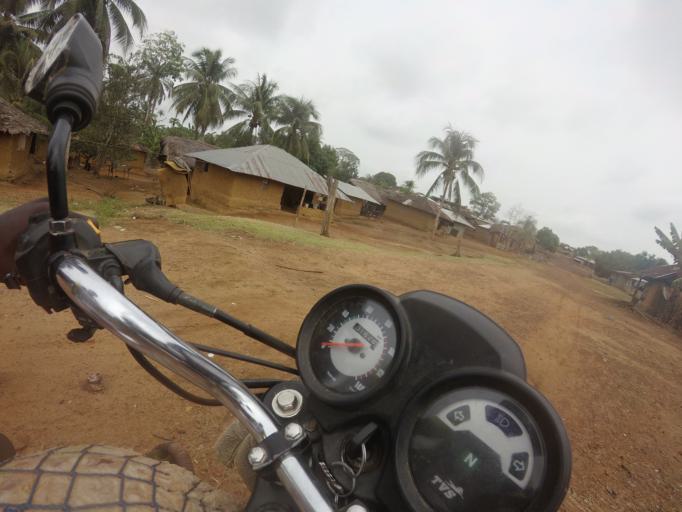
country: SL
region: Southern Province
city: Zimmi
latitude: 7.1622
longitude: -11.2430
